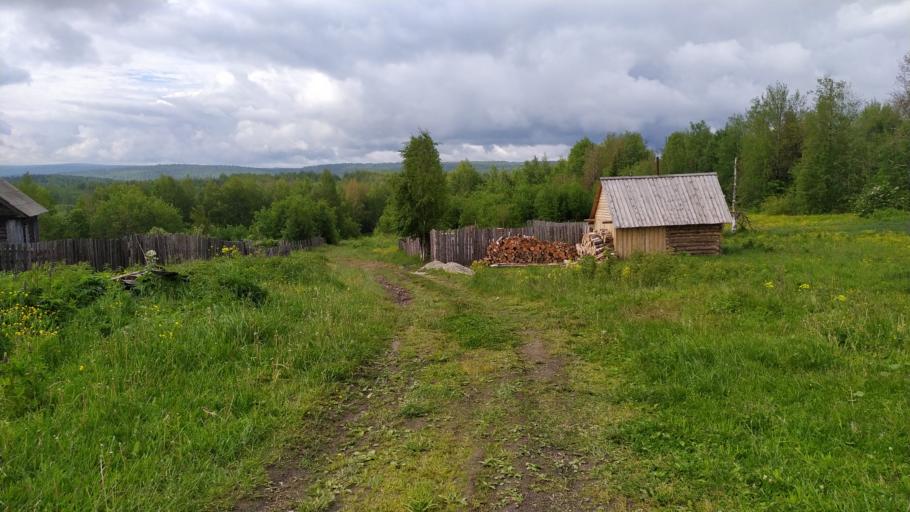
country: RU
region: Perm
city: Gremyachinsk
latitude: 58.5269
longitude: 57.8609
